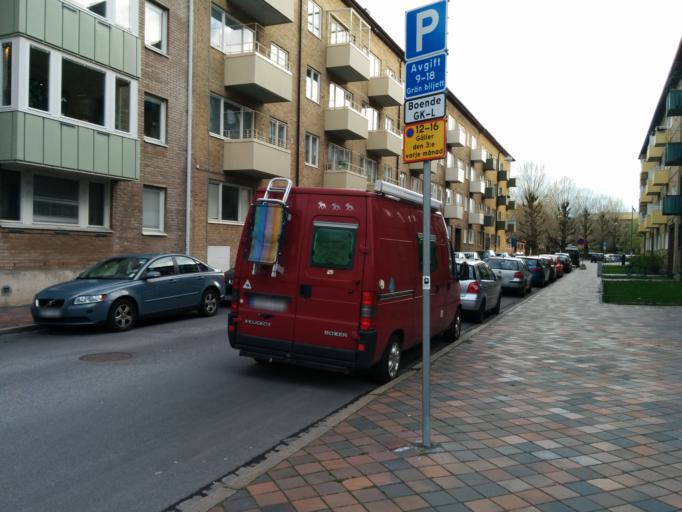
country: SE
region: Skane
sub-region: Malmo
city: Malmoe
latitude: 55.5949
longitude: 13.0200
